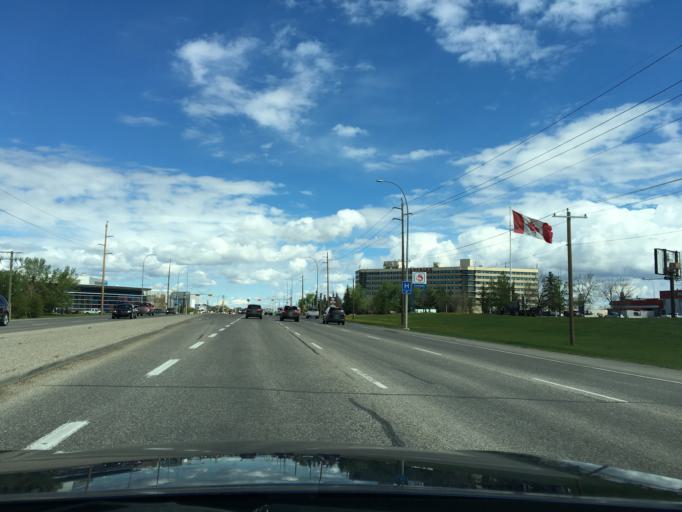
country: CA
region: Alberta
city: Calgary
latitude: 51.0796
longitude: -114.0017
